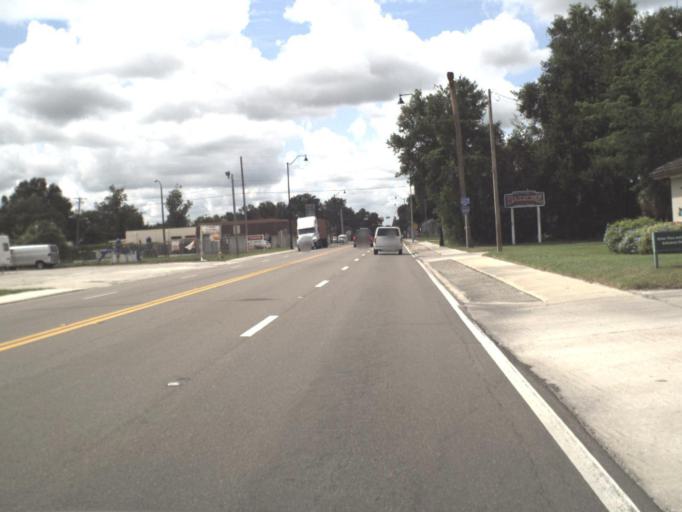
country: US
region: Florida
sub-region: Hardee County
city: Bowling Green
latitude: 27.6410
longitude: -81.8235
